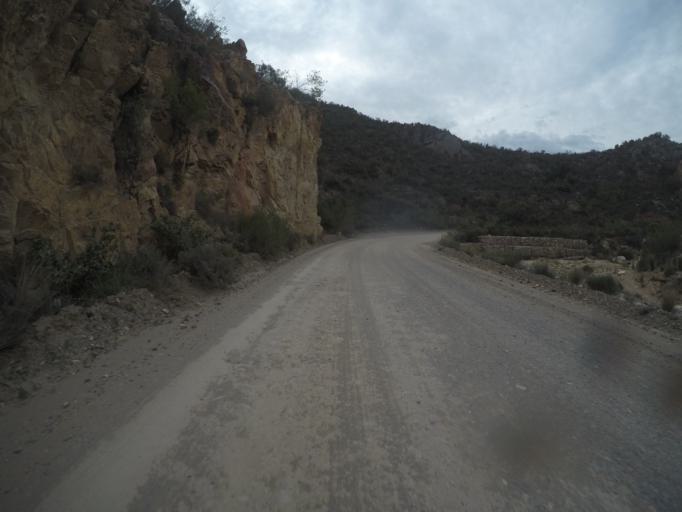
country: ZA
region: Eastern Cape
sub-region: Cacadu District Municipality
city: Willowmore
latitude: -33.5089
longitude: 23.6366
